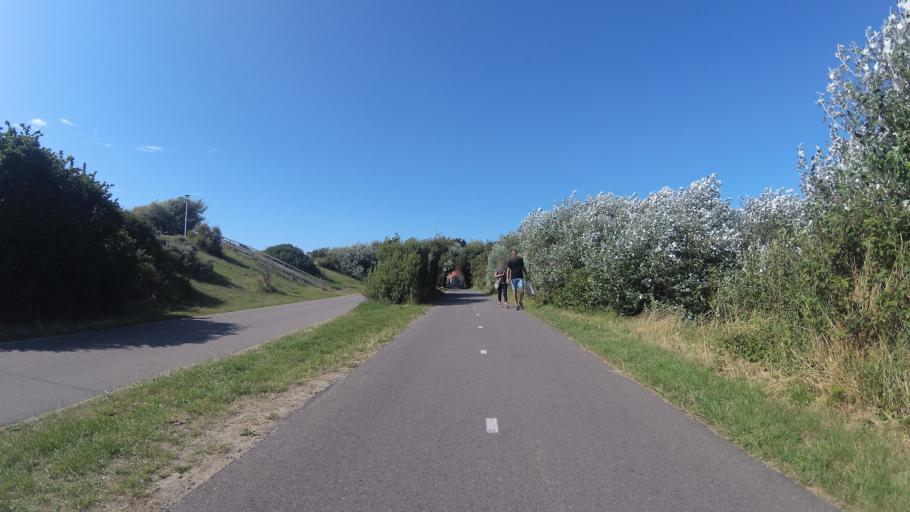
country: NL
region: Zeeland
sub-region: Gemeente Vlissingen
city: Vlissingen
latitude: 51.5248
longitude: 3.4418
